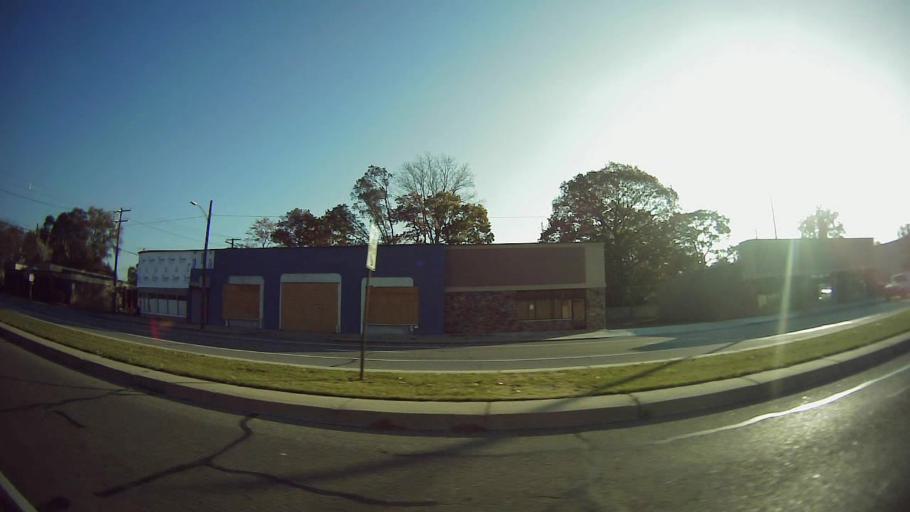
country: US
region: Michigan
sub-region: Oakland County
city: Ferndale
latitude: 42.4422
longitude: -83.1420
